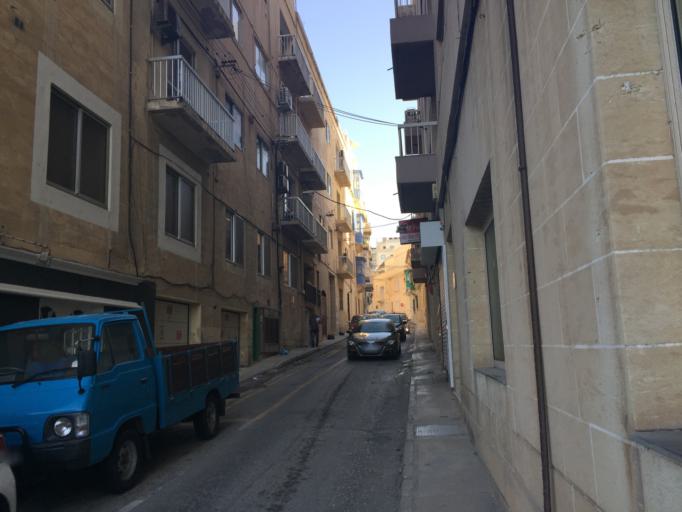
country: MT
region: Tas-Sliema
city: Sliema
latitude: 35.9152
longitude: 14.5040
